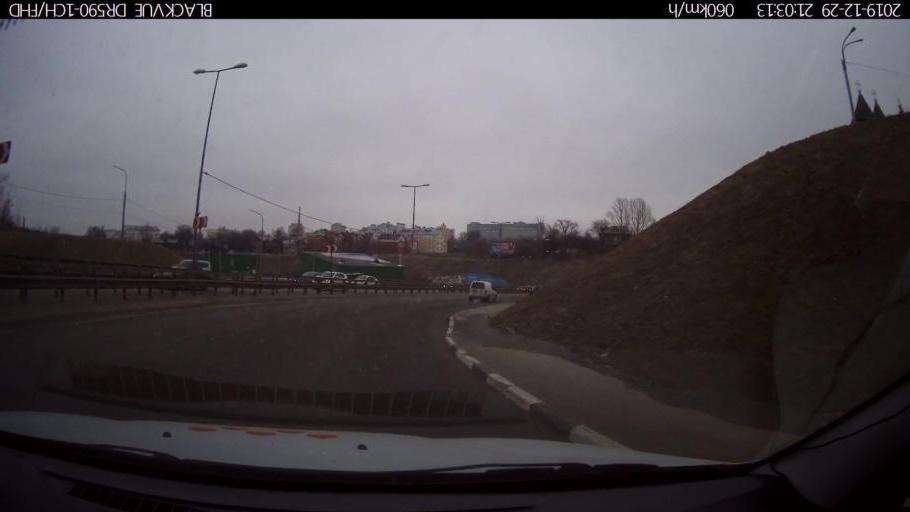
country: RU
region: Nizjnij Novgorod
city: Nizhniy Novgorod
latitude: 56.3156
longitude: 43.9753
